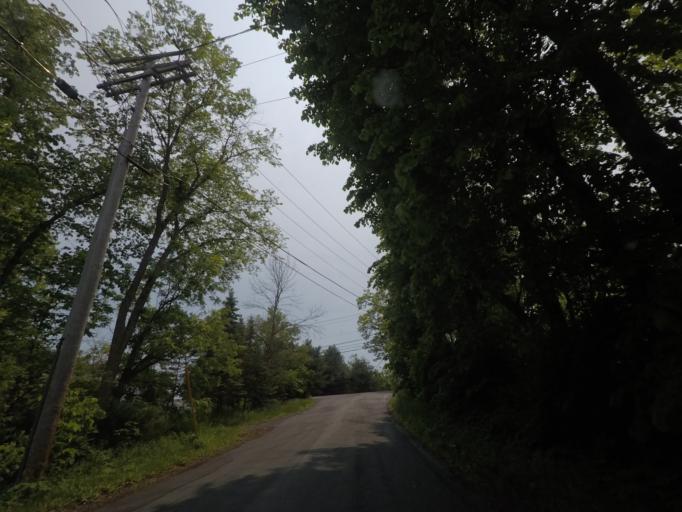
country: US
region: New York
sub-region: Rensselaer County
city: Castleton-on-Hudson
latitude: 42.5260
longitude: -73.7160
